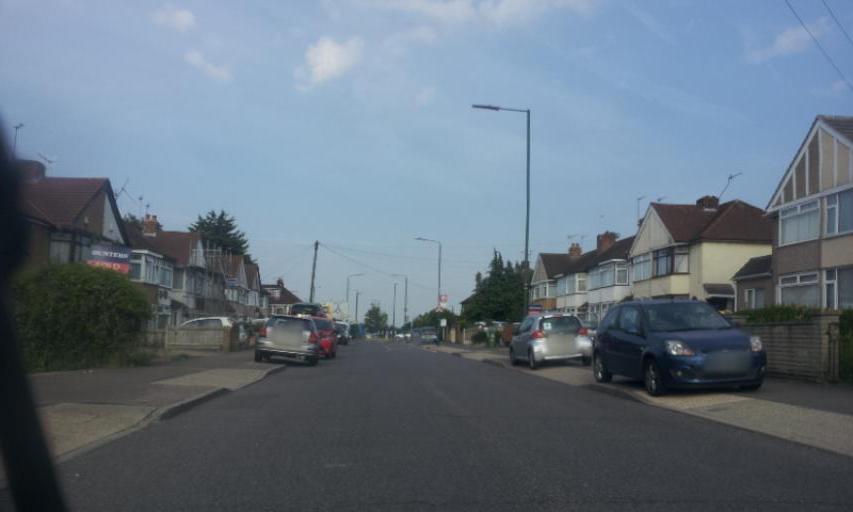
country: GB
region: England
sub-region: Greater London
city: Erith
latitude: 51.4636
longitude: 0.1800
